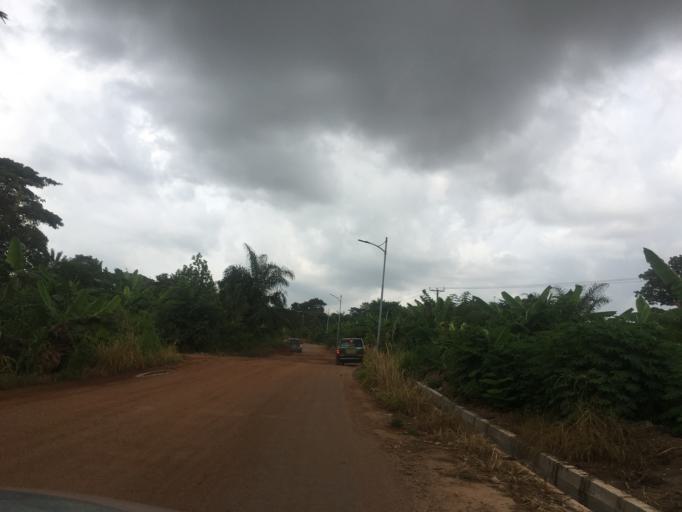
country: GH
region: Ashanti
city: Mamponteng
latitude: 6.6853
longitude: -1.5600
